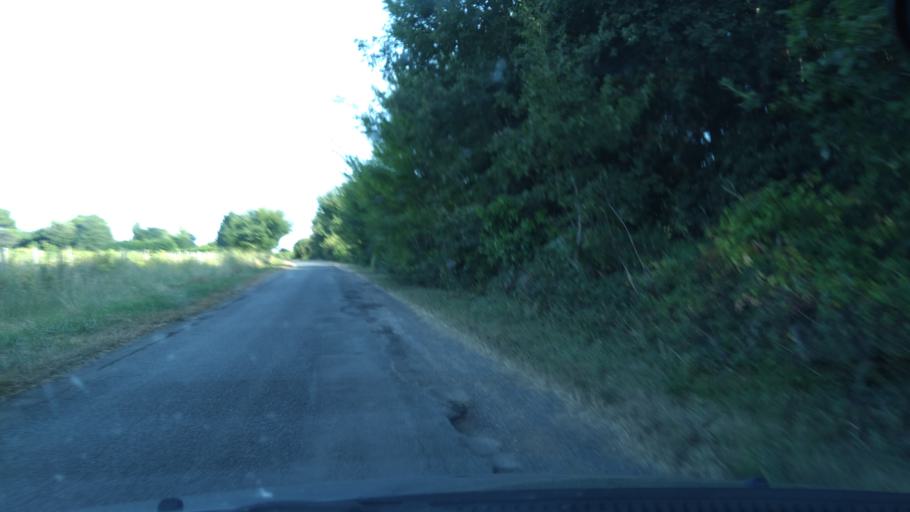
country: FR
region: Poitou-Charentes
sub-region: Departement de la Charente-Maritime
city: Dolus-d'Oleron
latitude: 45.9462
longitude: -1.3465
